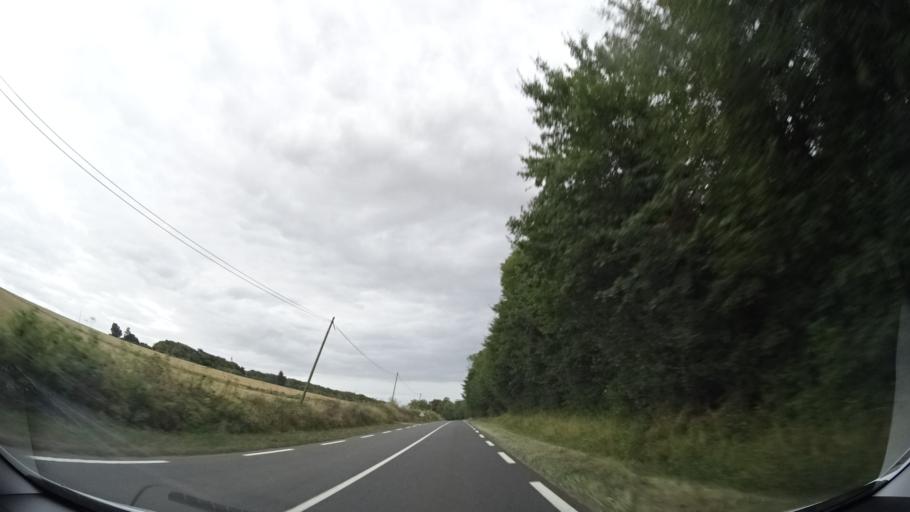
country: FR
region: Centre
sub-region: Departement du Loiret
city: Douchy
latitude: 47.9387
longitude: 3.0676
